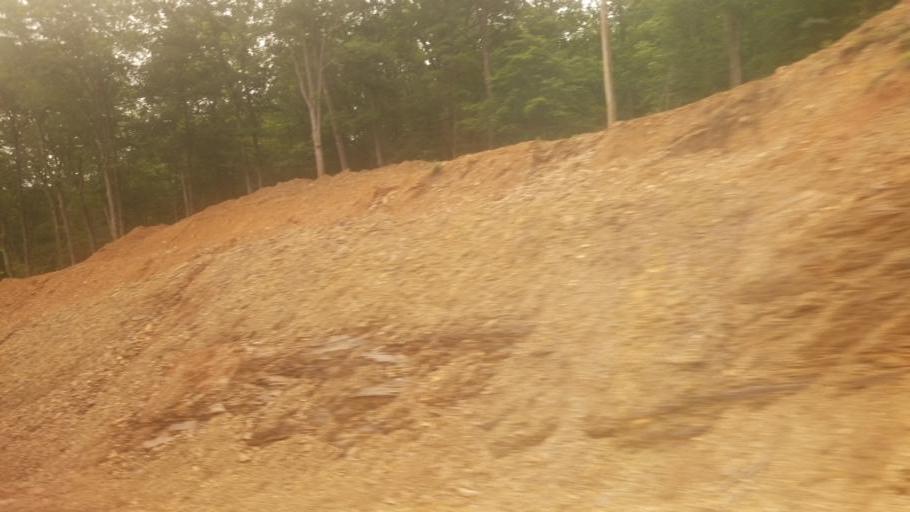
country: US
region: West Virginia
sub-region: Morgan County
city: Berkeley Springs
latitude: 39.5761
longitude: -78.4124
